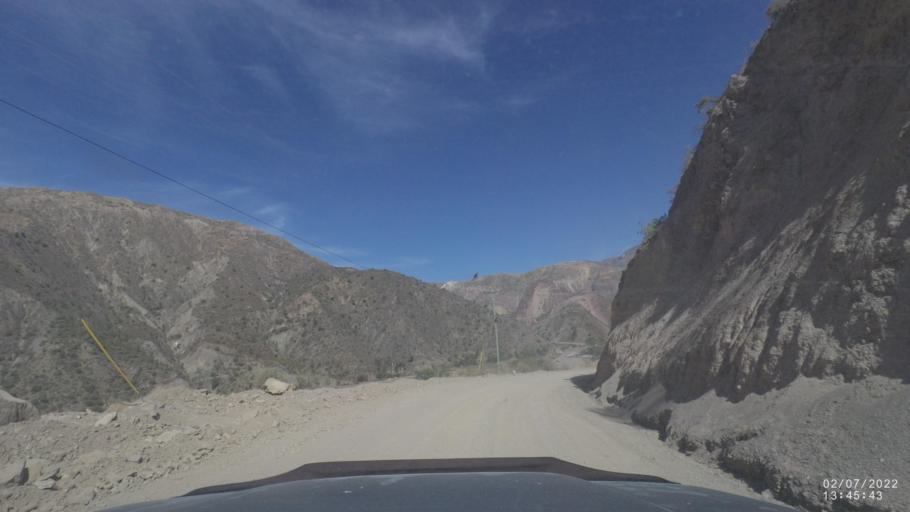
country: BO
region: Cochabamba
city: Irpa Irpa
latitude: -17.8101
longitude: -66.3648
